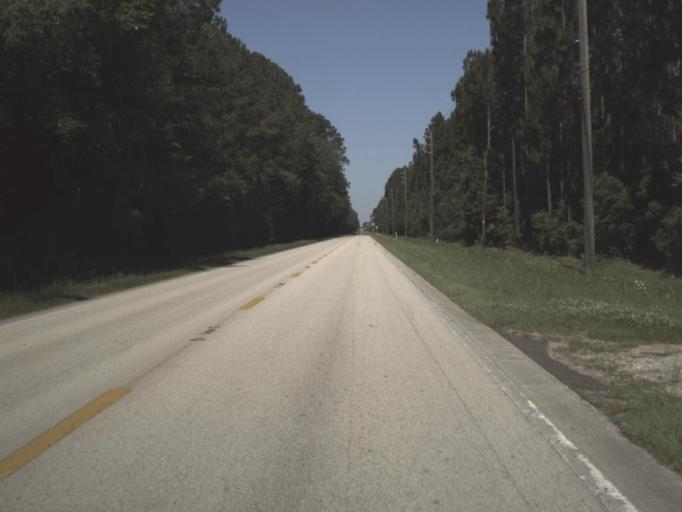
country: US
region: Florida
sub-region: Duval County
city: Baldwin
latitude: 30.3029
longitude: -81.9571
